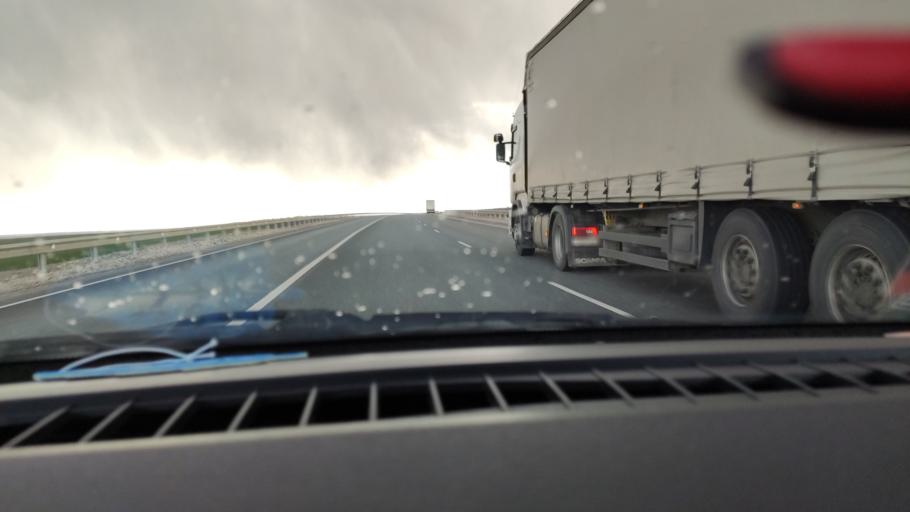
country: RU
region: Saratov
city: Yelshanka
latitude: 51.8333
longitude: 46.4653
